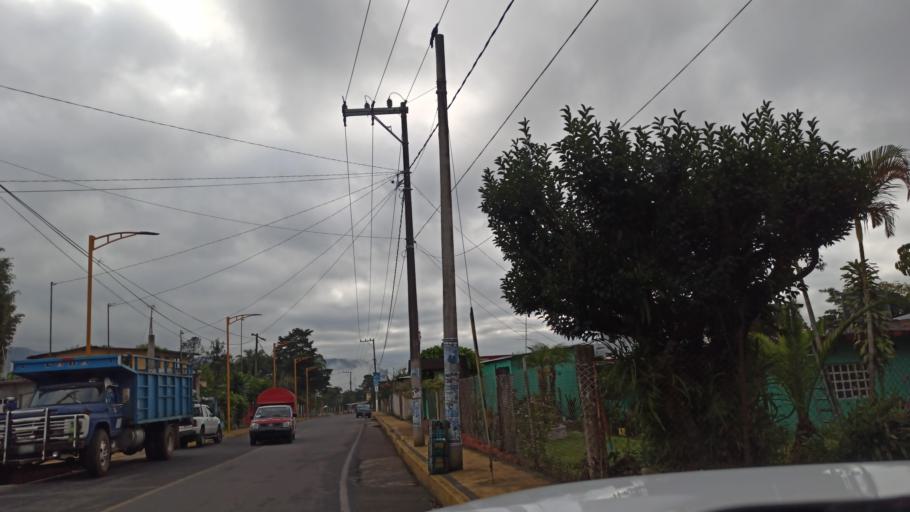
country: MX
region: Veracruz
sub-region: Chocaman
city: San Jose Neria
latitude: 19.0028
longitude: -97.0051
